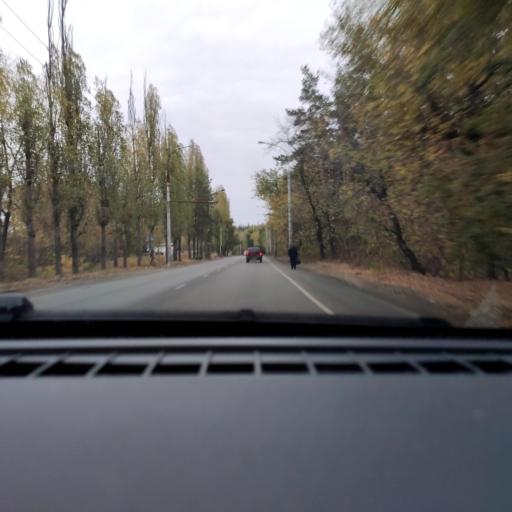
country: RU
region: Voronezj
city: Somovo
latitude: 51.7023
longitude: 39.2850
